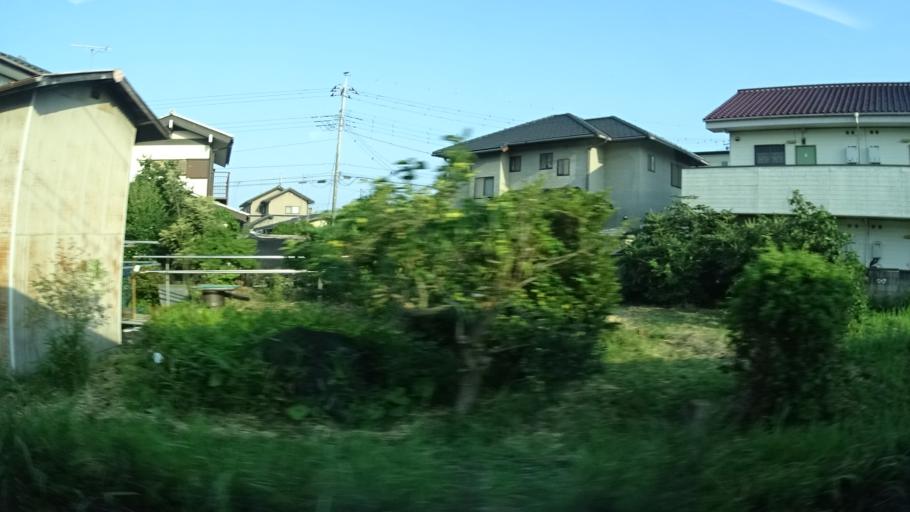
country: JP
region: Ibaraki
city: Funaishikawa
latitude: 36.4735
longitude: 140.5764
